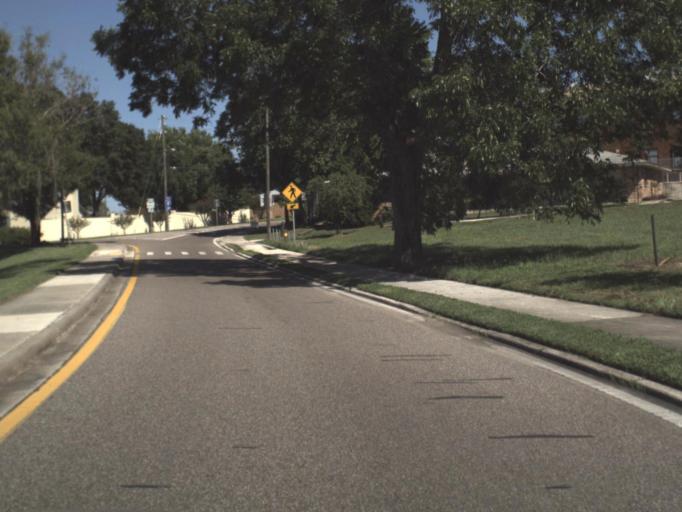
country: US
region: Florida
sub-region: Polk County
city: Auburndale
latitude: 28.0693
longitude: -81.7880
